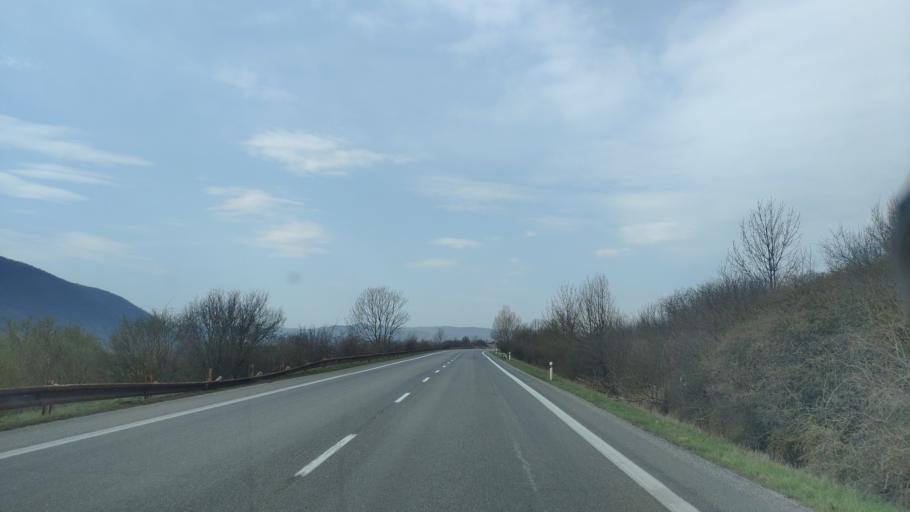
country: SK
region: Kosicky
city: Roznava
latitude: 48.5955
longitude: 20.7030
